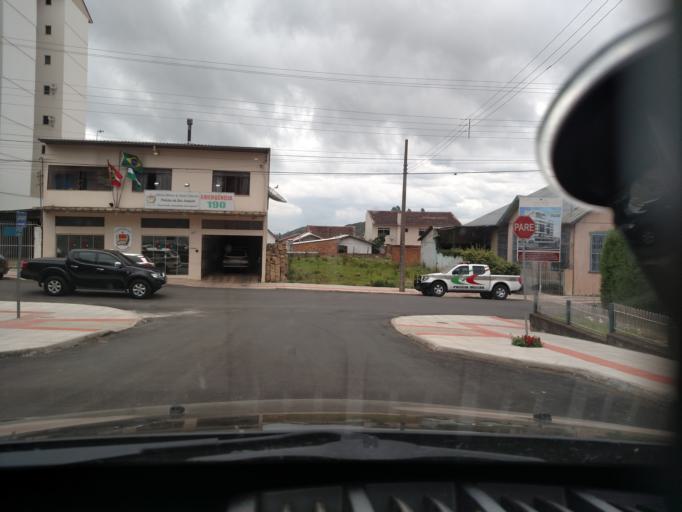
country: BR
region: Santa Catarina
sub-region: Sao Joaquim
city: Sao Joaquim
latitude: -28.2940
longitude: -49.9333
